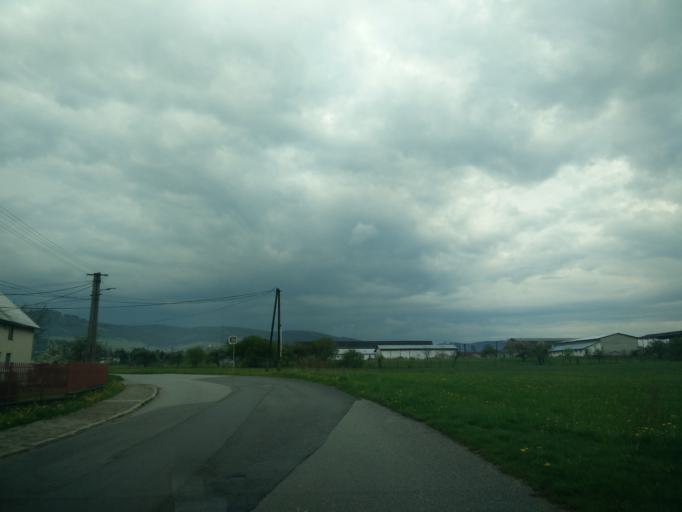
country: SK
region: Banskobystricky
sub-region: Okres Ziar nad Hronom
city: Kremnica
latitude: 48.8445
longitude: 18.8628
